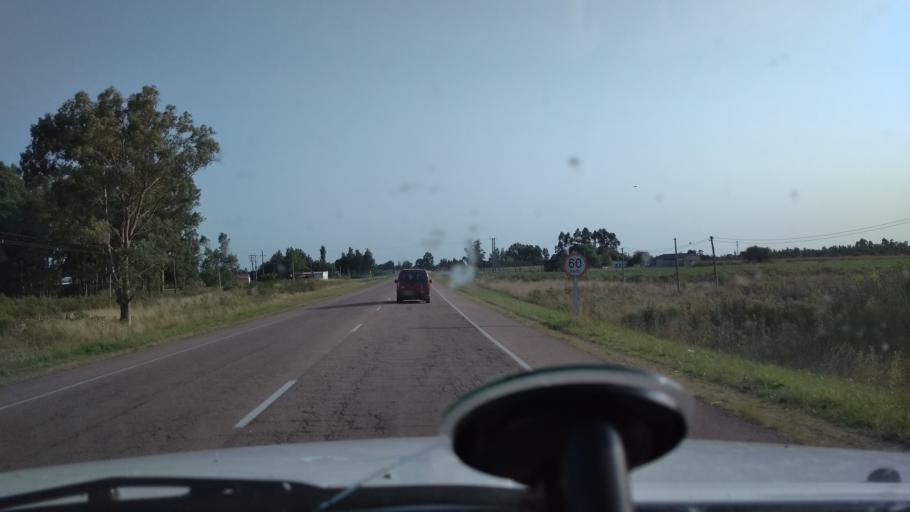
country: UY
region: Canelones
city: Sauce
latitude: -34.6344
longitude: -56.0521
